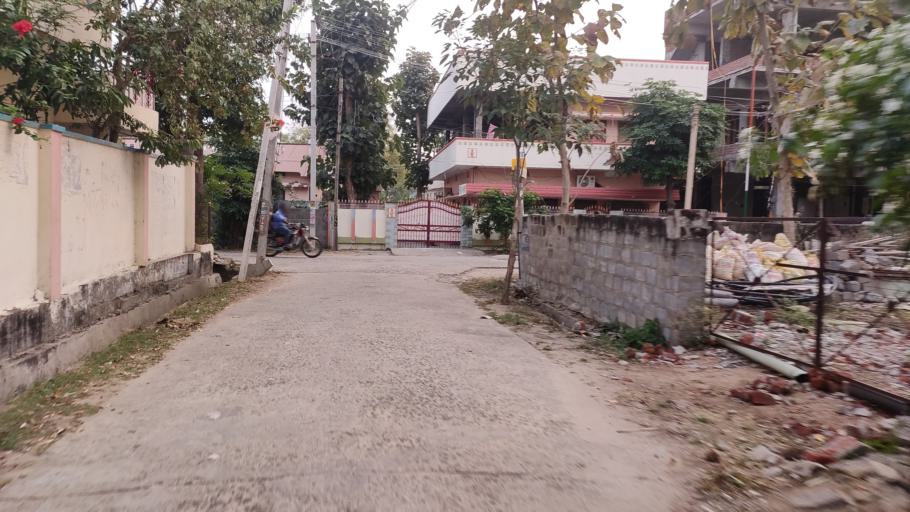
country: IN
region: Telangana
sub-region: Warangal
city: Warangal
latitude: 17.9626
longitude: 79.6022
